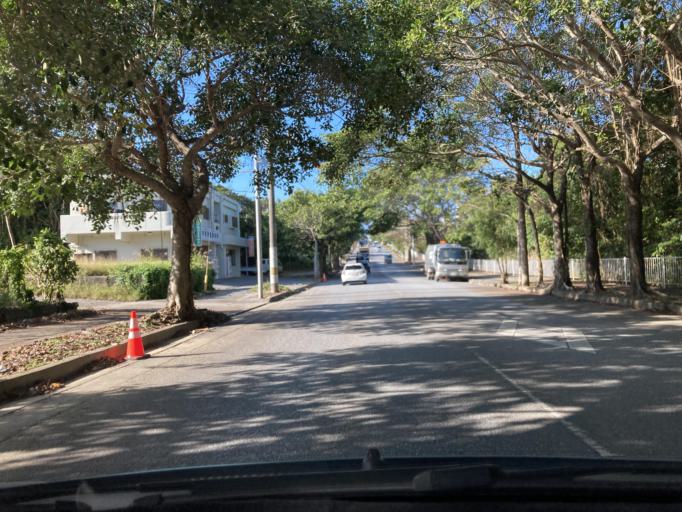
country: JP
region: Okinawa
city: Gushikawa
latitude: 26.3650
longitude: 127.8417
